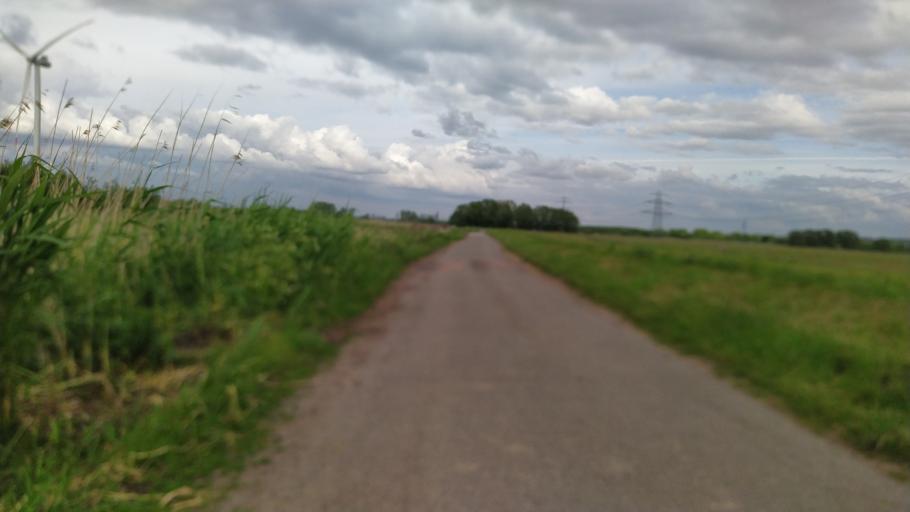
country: DE
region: Lower Saxony
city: Neu Wulmstorf
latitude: 53.4947
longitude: 9.8479
